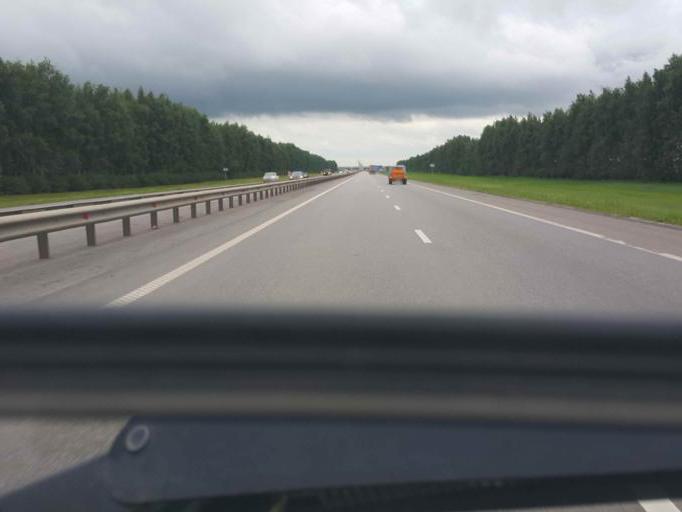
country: RU
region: Tambov
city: Zavoronezhskoye
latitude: 52.8495
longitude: 40.8043
